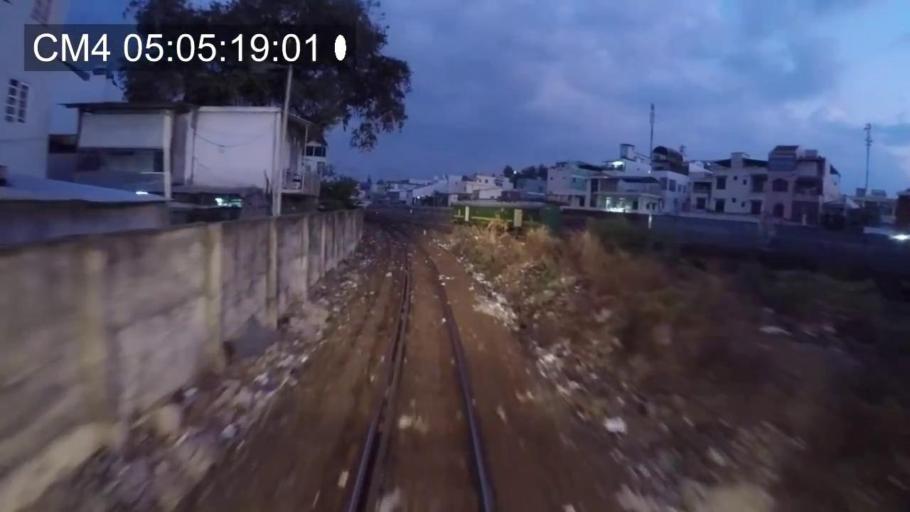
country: VN
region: Khanh Hoa
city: Nha Trang
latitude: 12.2703
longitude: 109.1754
